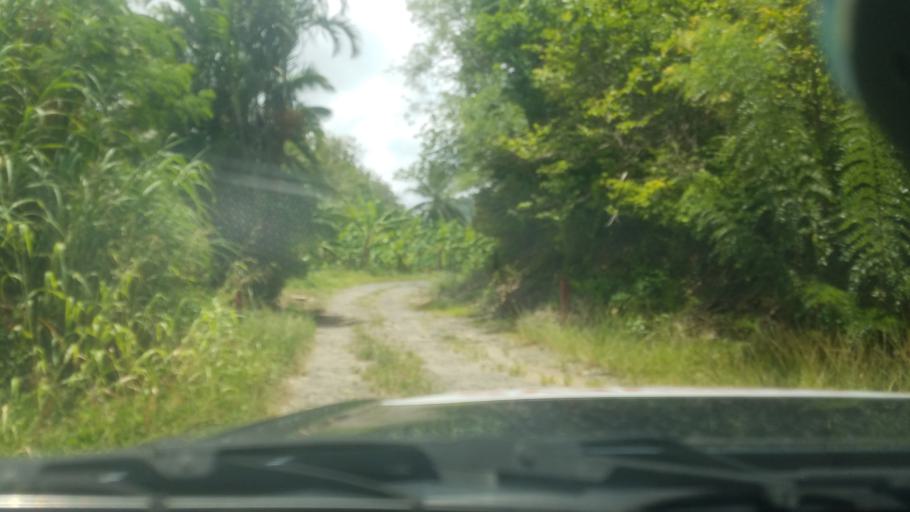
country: LC
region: Praslin
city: Praslin
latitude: 13.8675
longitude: -60.9014
